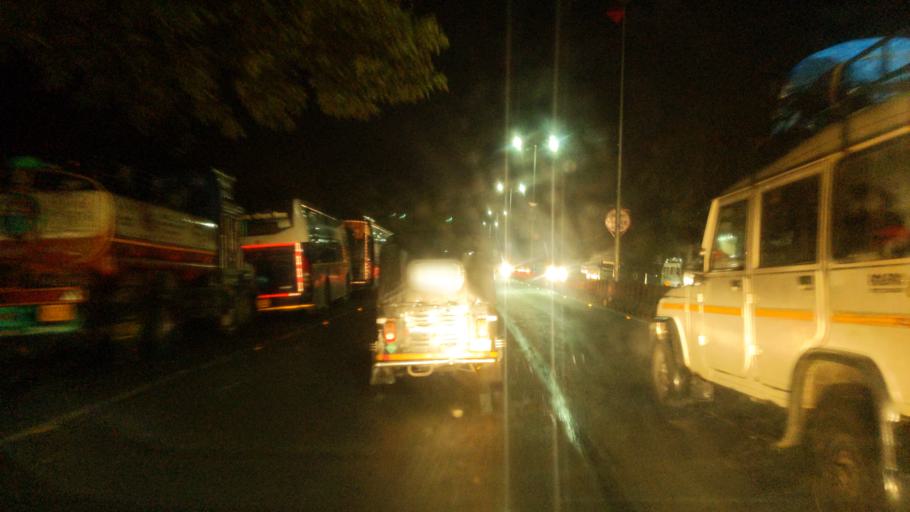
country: IN
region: Uttarakhand
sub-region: Naini Tal
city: Haldwani
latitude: 29.2593
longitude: 79.5433
